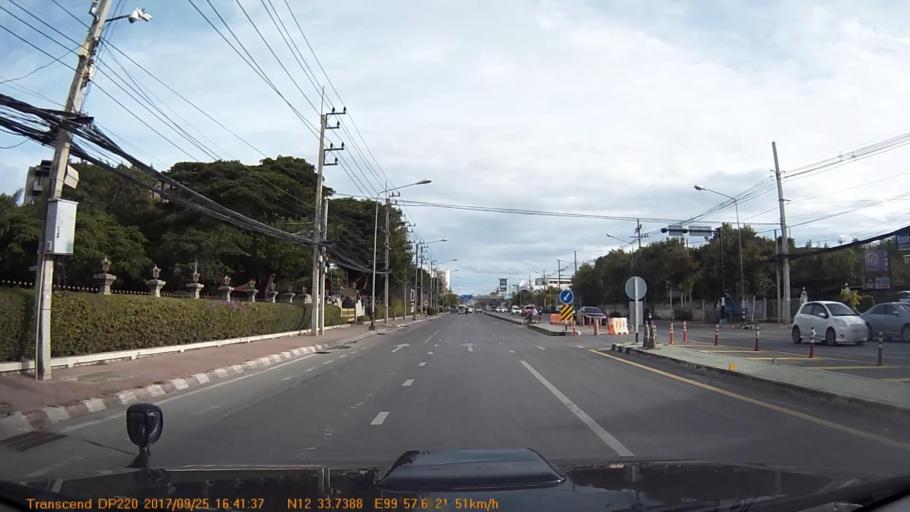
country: TH
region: Prachuap Khiri Khan
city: Hua Hin
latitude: 12.5622
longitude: 99.9602
